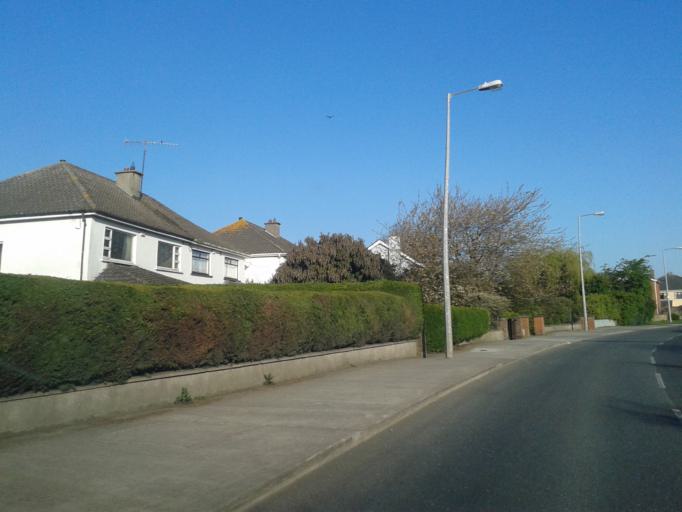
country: IE
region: Leinster
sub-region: Fingal County
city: Swords
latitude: 53.4655
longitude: -6.2366
